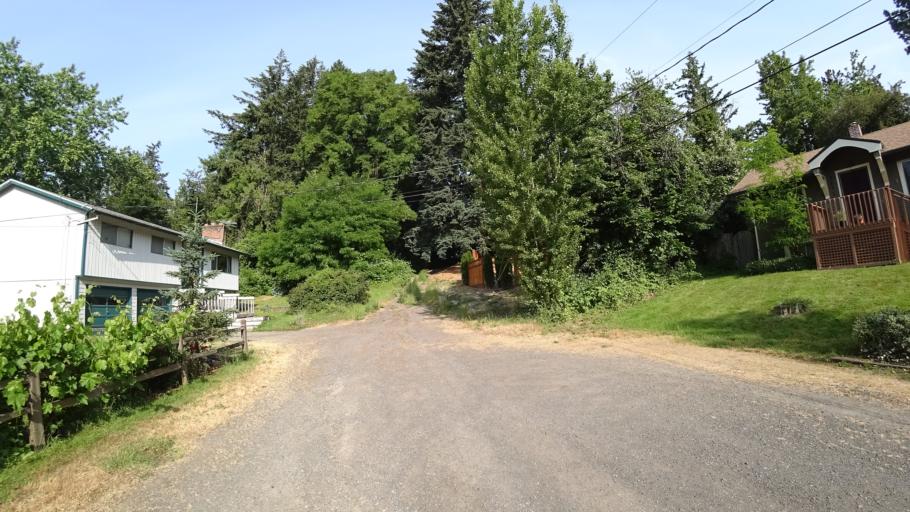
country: US
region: Oregon
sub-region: Washington County
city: Garden Home-Whitford
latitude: 45.4633
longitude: -122.7149
